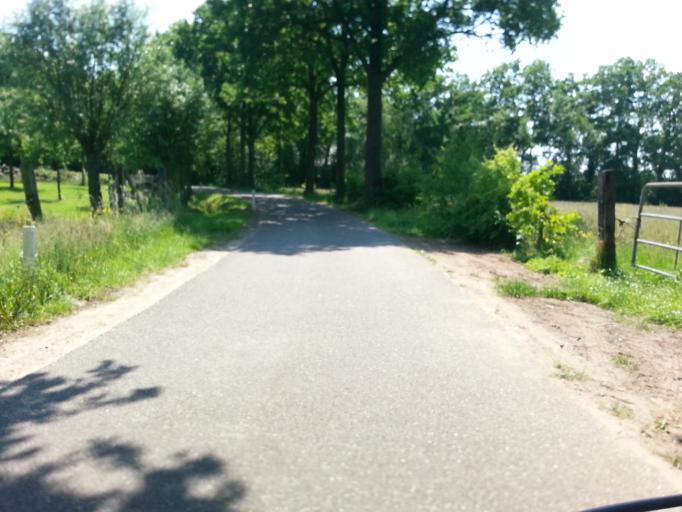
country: NL
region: Gelderland
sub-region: Gemeente Barneveld
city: Terschuur
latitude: 52.1434
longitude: 5.4944
